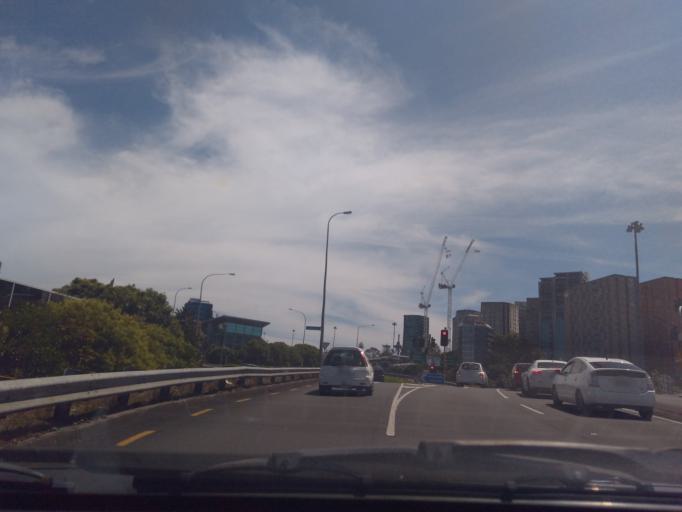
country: NZ
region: Auckland
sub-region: Auckland
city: Auckland
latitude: -36.8559
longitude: 174.7704
